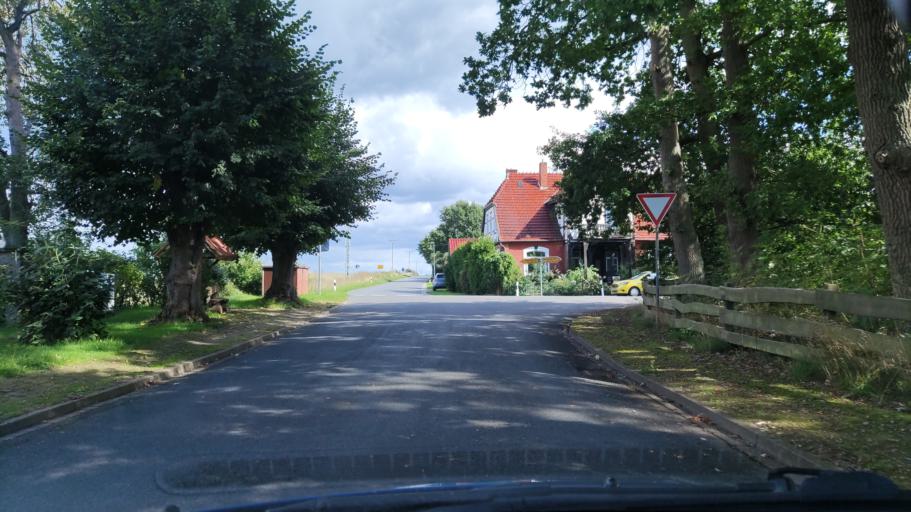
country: DE
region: Lower Saxony
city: Weste
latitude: 53.0595
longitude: 10.7059
